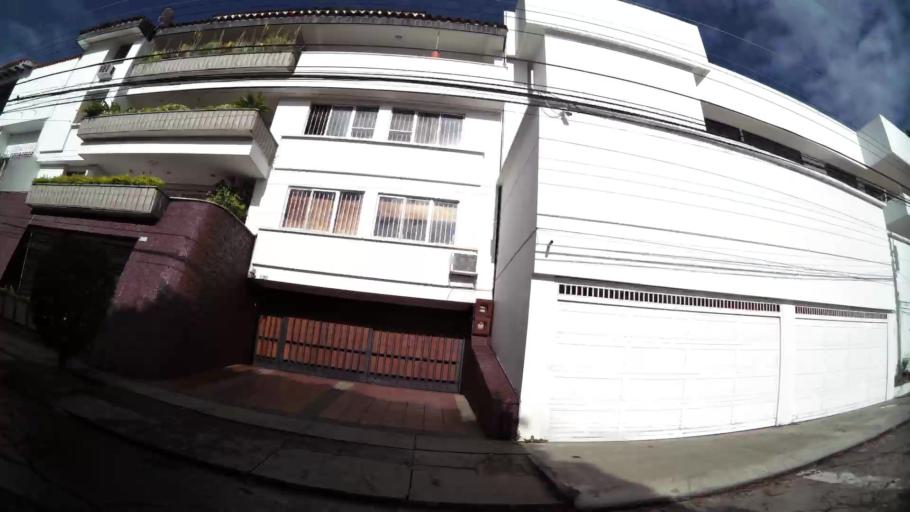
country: CO
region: Valle del Cauca
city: Cali
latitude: 3.4389
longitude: -76.5473
